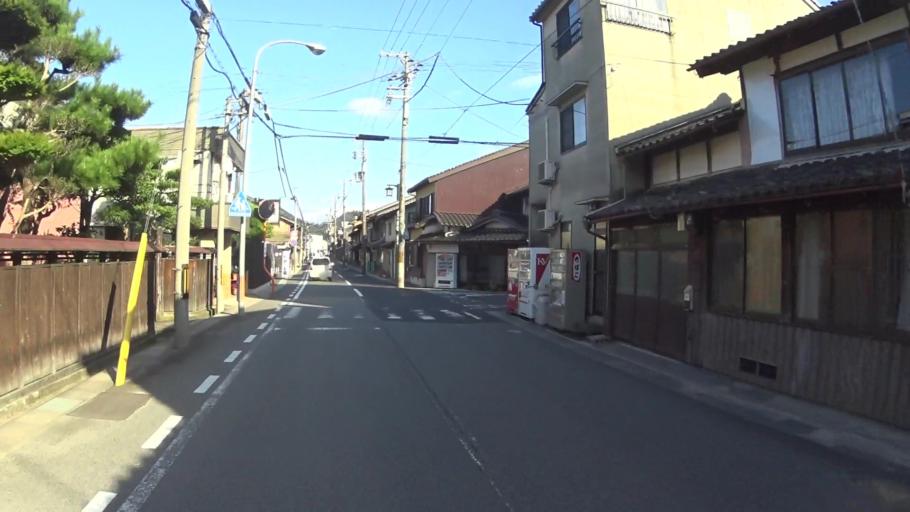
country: JP
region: Hyogo
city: Toyooka
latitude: 35.6073
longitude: 134.8945
